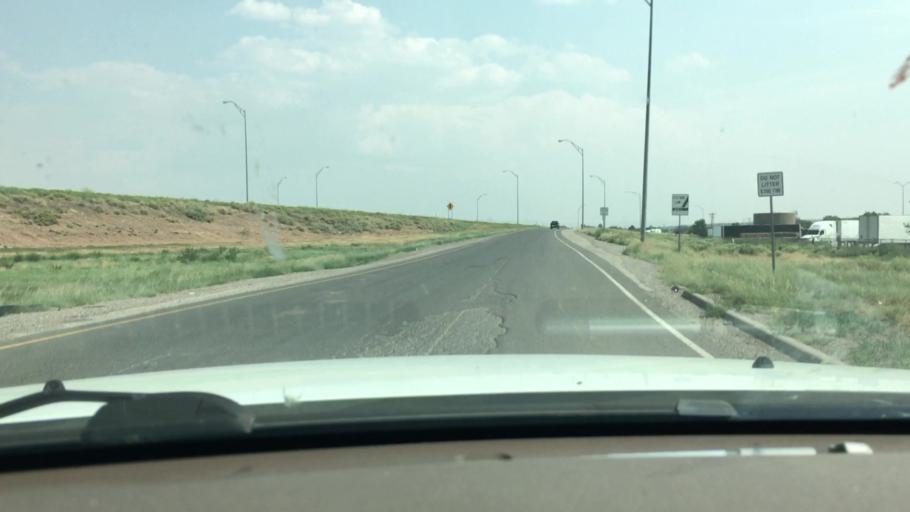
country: US
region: New Mexico
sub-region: Cibola County
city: Milan
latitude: 35.1818
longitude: -107.9023
